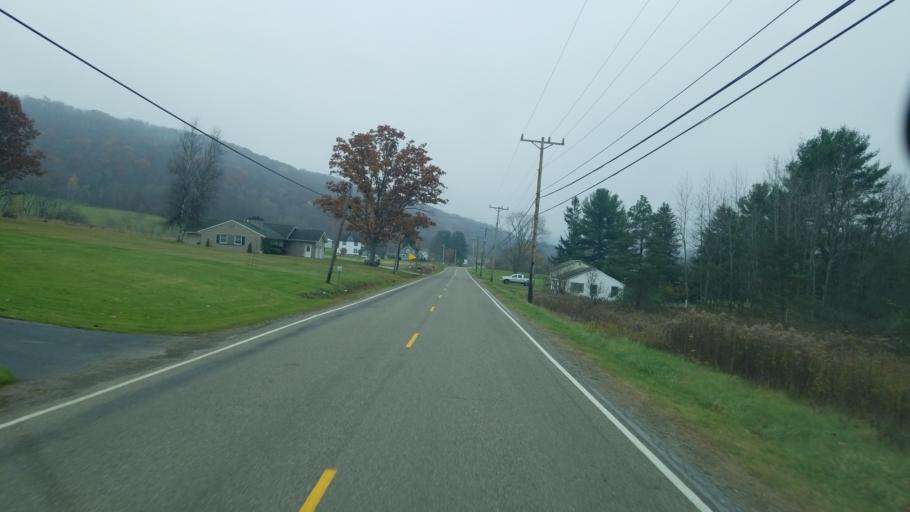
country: US
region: Pennsylvania
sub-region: McKean County
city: Smethport
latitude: 41.8744
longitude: -78.4829
